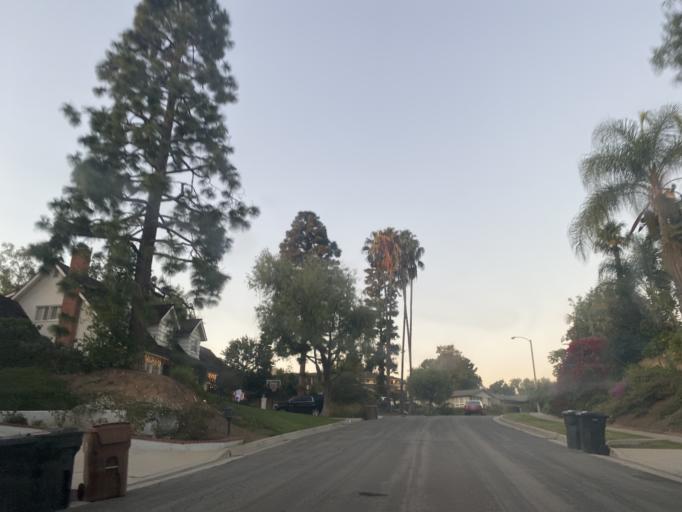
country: US
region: California
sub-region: Orange County
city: Fullerton
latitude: 33.8848
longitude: -117.9045
